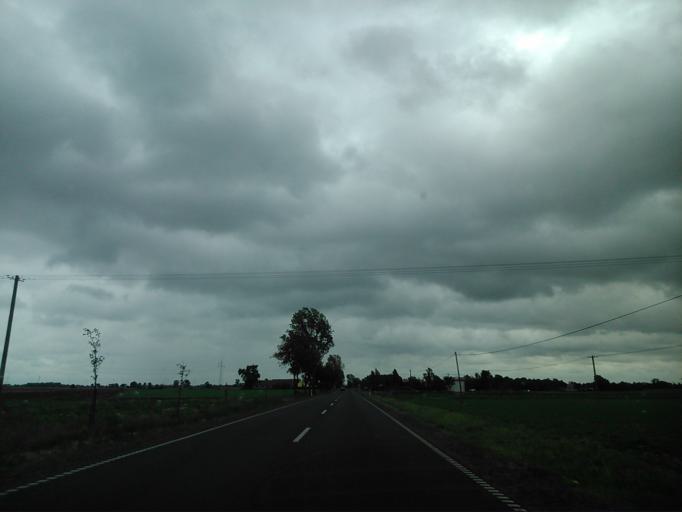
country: PL
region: Kujawsko-Pomorskie
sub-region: Powiat inowroclawski
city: Kruszwica
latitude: 52.6611
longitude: 18.3603
